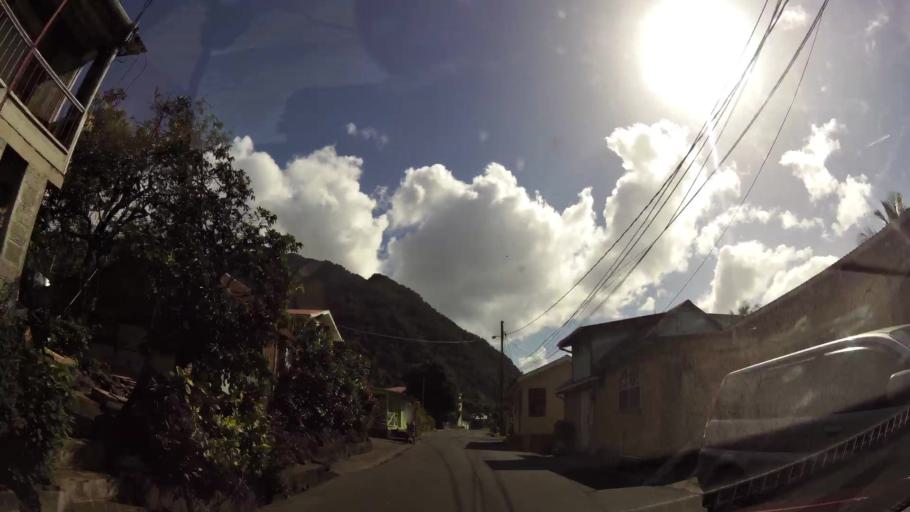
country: DM
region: Saint Luke
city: Pointe Michel
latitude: 15.2789
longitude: -61.3743
